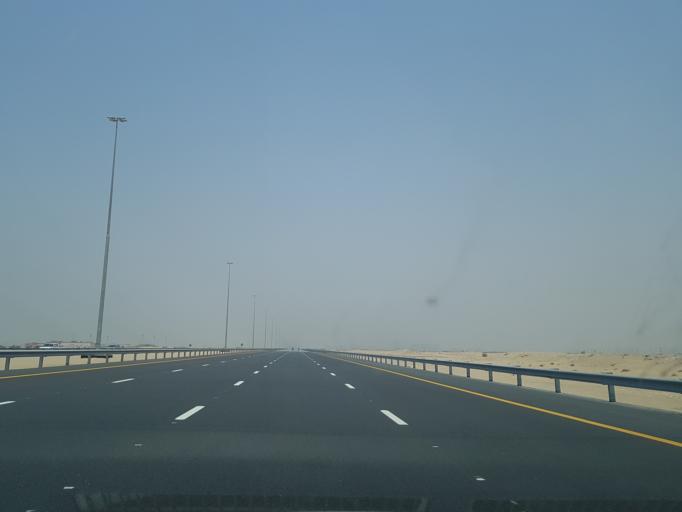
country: AE
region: Dubai
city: Dubai
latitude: 25.0723
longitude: 55.3252
